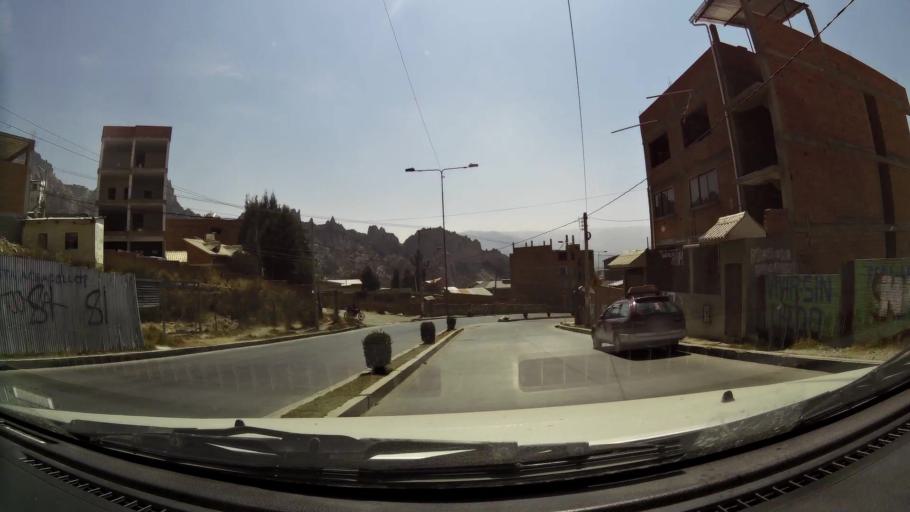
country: BO
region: La Paz
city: La Paz
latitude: -16.5305
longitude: -68.1293
